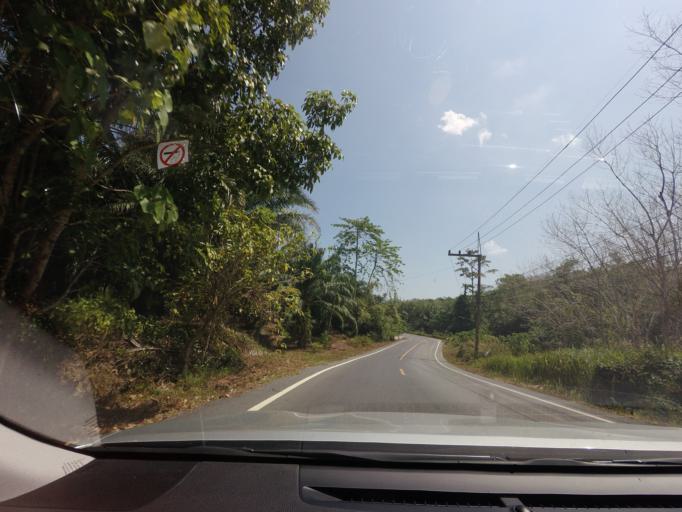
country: TH
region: Phangnga
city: Takua Thung
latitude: 8.2513
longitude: 98.3983
